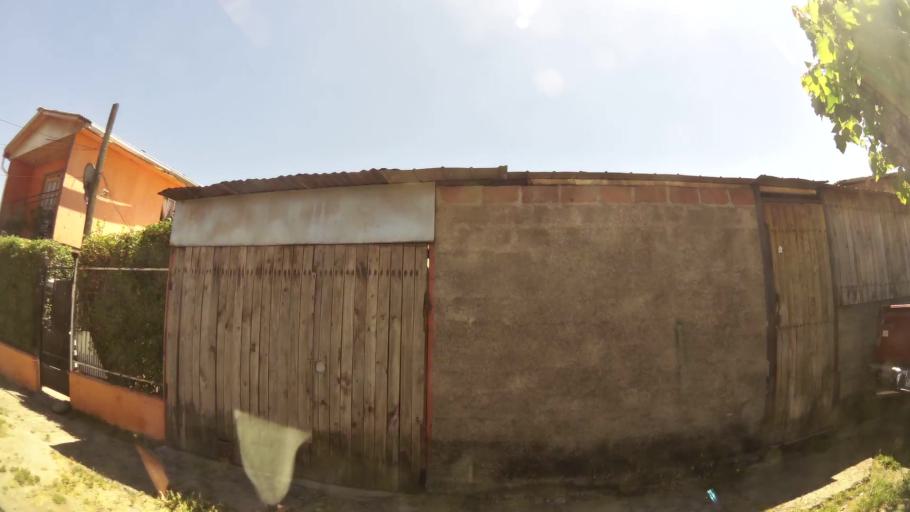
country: CL
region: Santiago Metropolitan
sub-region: Provincia de Santiago
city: La Pintana
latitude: -33.5681
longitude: -70.6656
